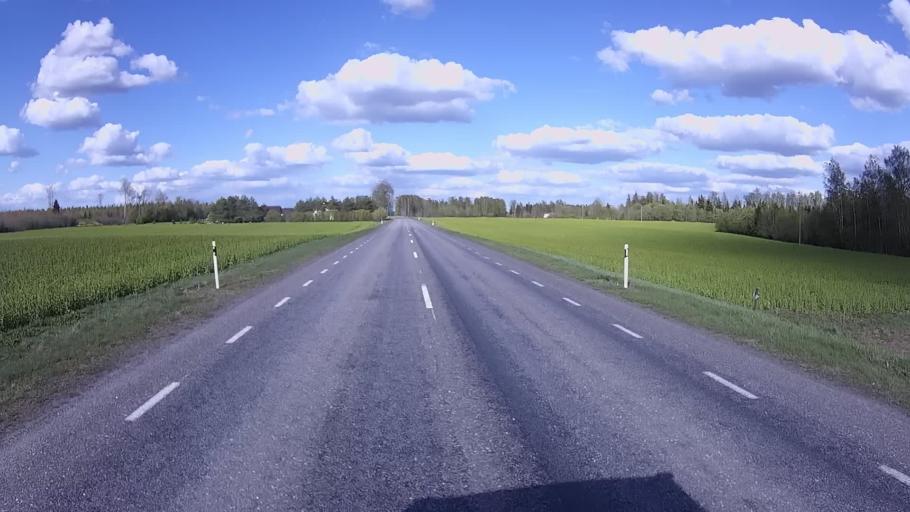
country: EE
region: Jogevamaa
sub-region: Poltsamaa linn
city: Poltsamaa
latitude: 58.7039
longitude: 26.1562
